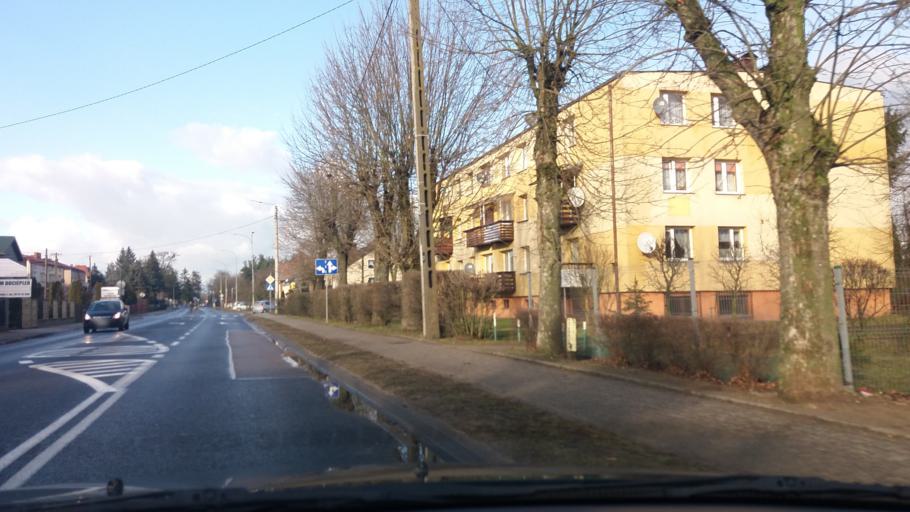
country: PL
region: Masovian Voivodeship
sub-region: Powiat przasnyski
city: Chorzele
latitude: 53.2640
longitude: 20.8974
